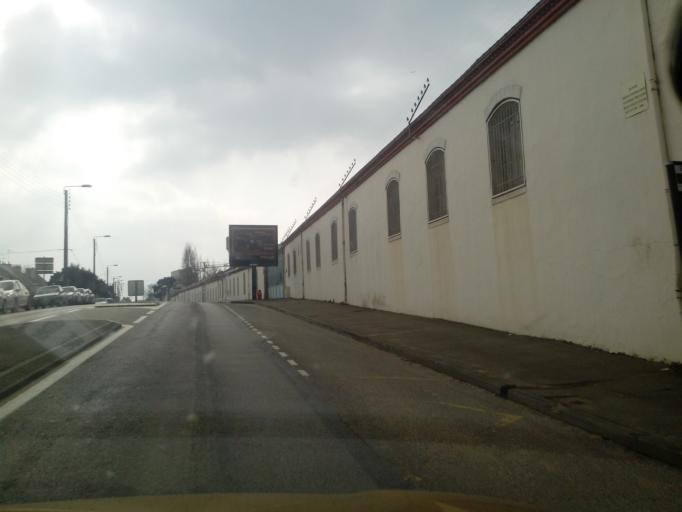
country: FR
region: Brittany
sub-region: Departement du Morbihan
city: Vannes
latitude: 47.6669
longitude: -2.7358
